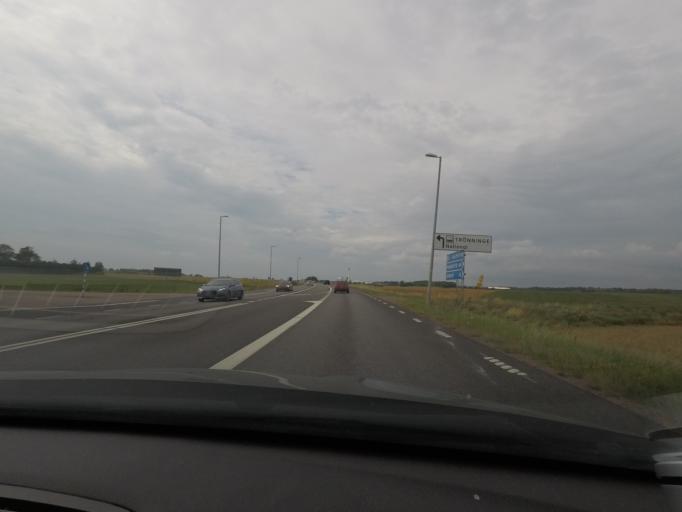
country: SE
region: Halland
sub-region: Halmstads Kommun
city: Troenninge
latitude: 56.6226
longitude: 12.9535
